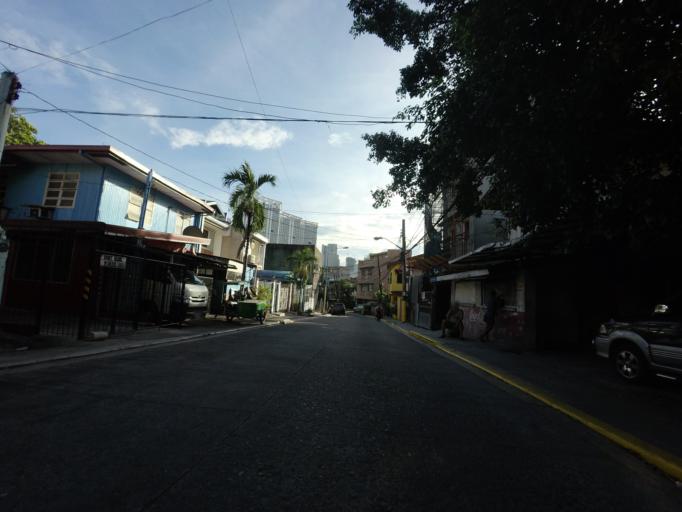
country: PH
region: Metro Manila
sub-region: Mandaluyong
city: Mandaluyong City
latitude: 14.5715
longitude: 121.0409
